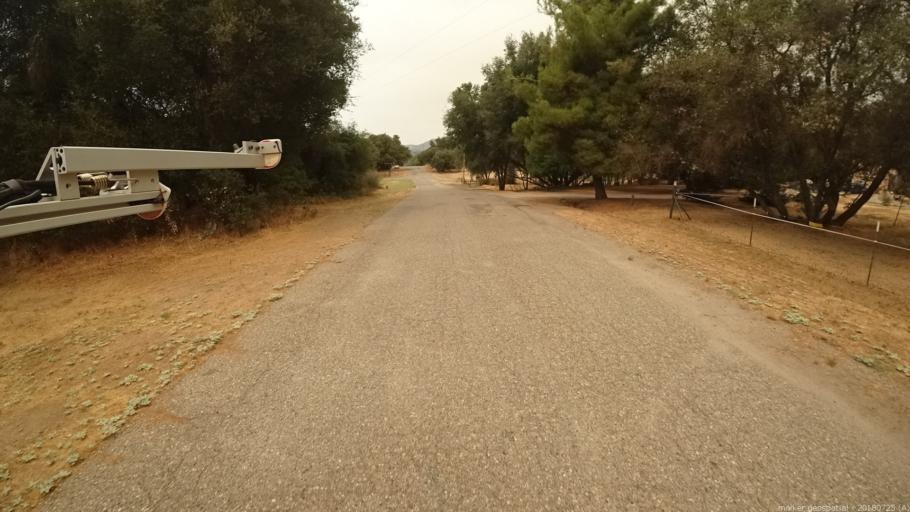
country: US
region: California
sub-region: Madera County
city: Coarsegold
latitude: 37.2142
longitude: -119.6736
